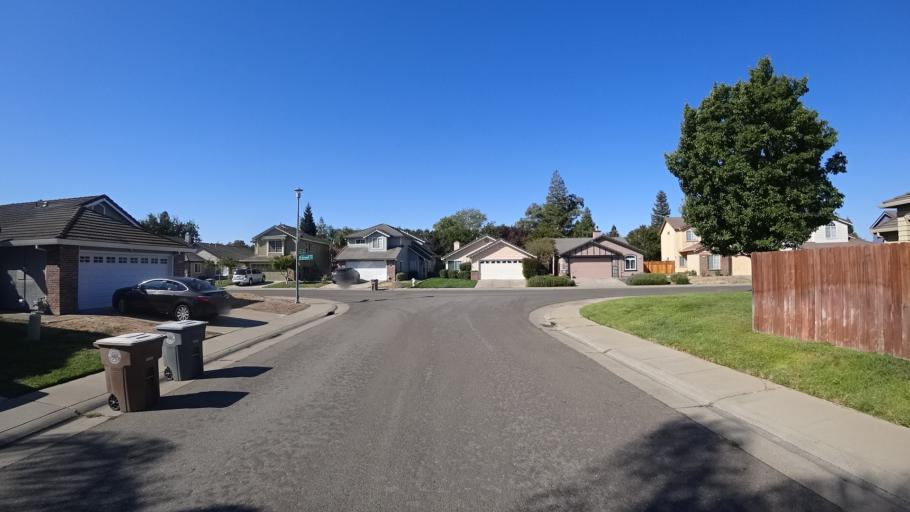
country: US
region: California
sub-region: Sacramento County
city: Laguna
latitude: 38.4362
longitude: -121.4416
